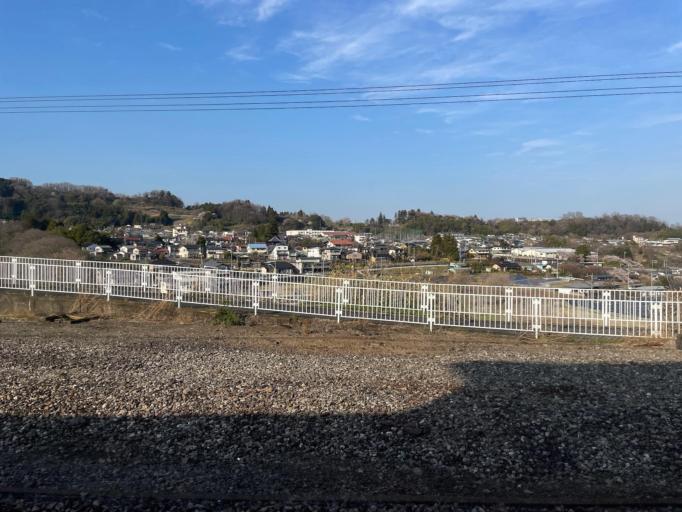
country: JP
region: Gunma
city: Annaka
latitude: 36.3082
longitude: 138.7994
